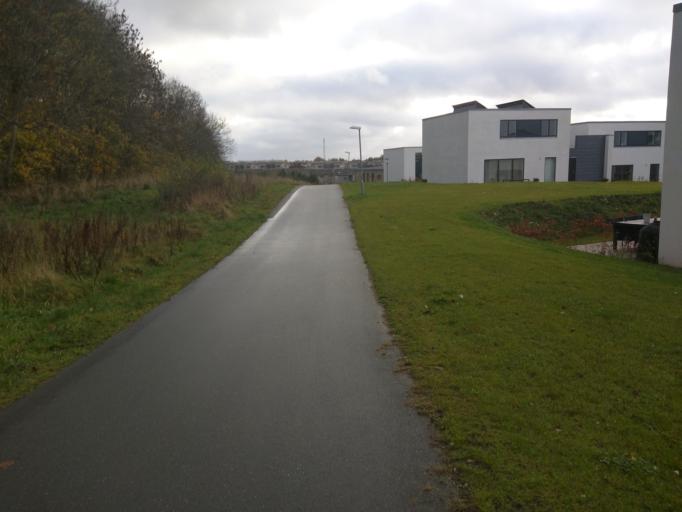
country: DK
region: Central Jutland
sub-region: Viborg Kommune
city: Viborg
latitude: 56.4417
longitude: 9.3683
